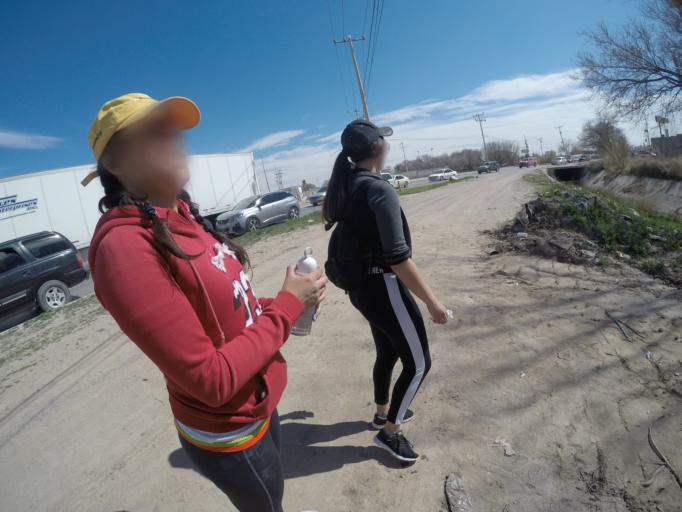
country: US
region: Texas
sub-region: El Paso County
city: Socorro
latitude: 31.6484
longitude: -106.3531
